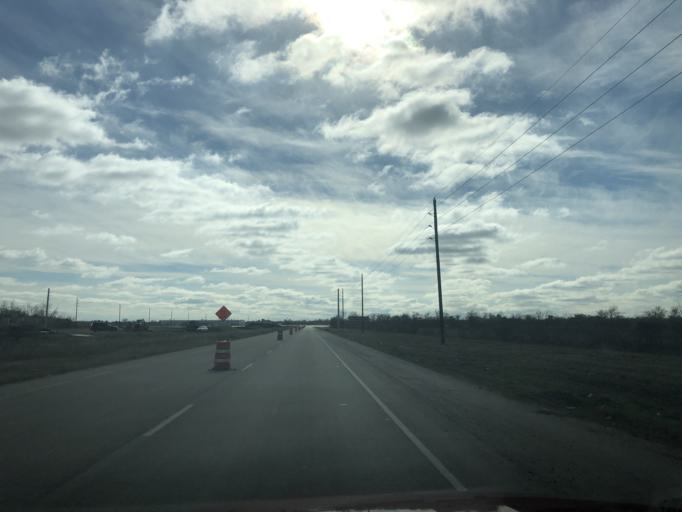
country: US
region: Texas
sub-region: Chambers County
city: Mont Belvieu
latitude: 29.8220
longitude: -94.8653
